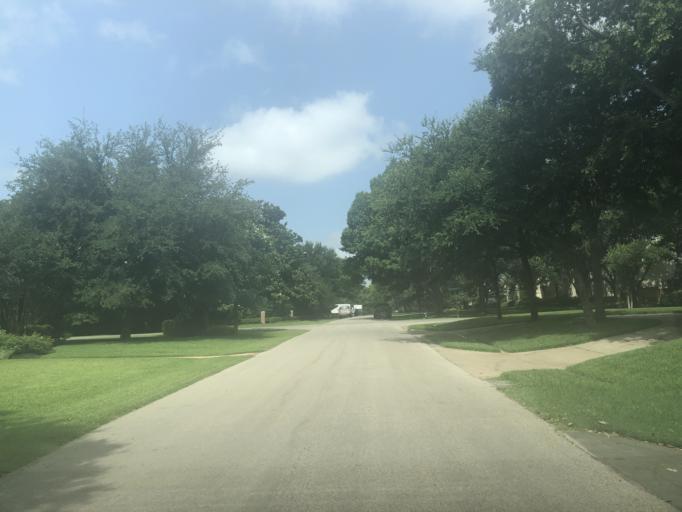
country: US
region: Texas
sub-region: Dallas County
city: University Park
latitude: 32.8687
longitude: -96.8334
